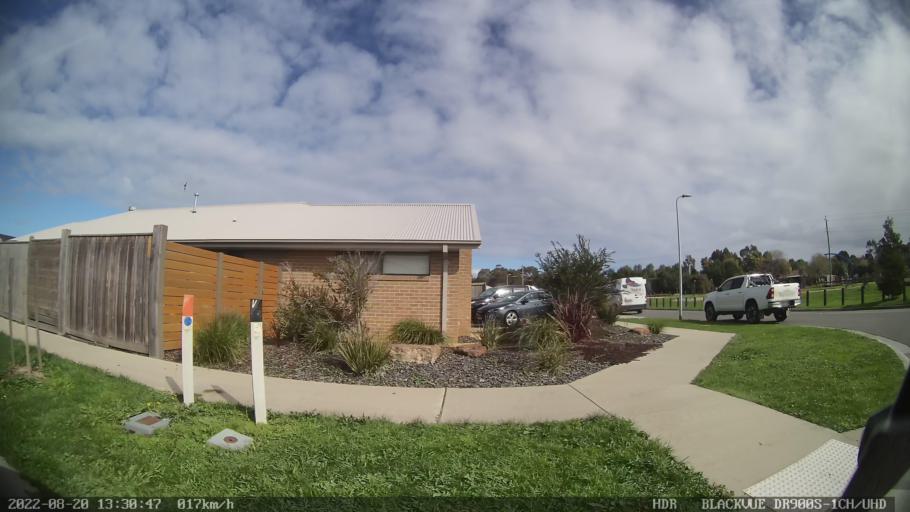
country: AU
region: Victoria
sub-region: Bass Coast
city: North Wonthaggi
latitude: -38.6000
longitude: 145.6128
